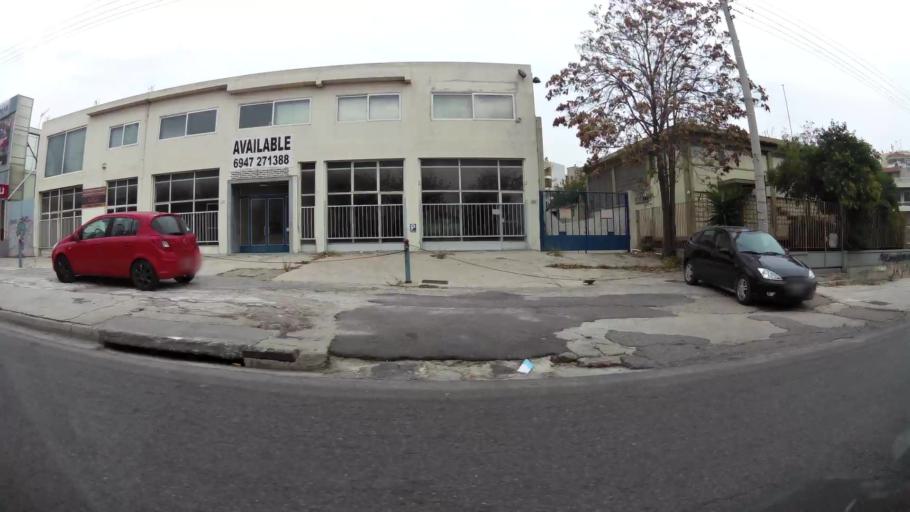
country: GR
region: Attica
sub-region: Nomarchia Athinas
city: Chaidari
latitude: 38.0111
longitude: 23.6684
